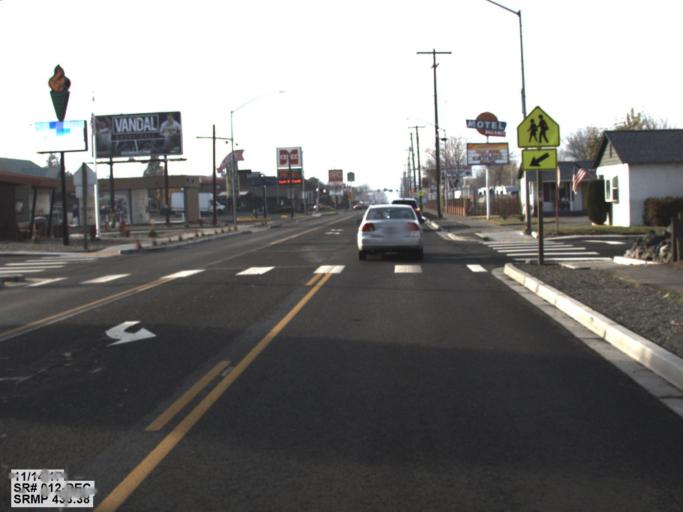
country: US
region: Washington
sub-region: Asotin County
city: Clarkston
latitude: 46.4199
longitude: -117.0532
